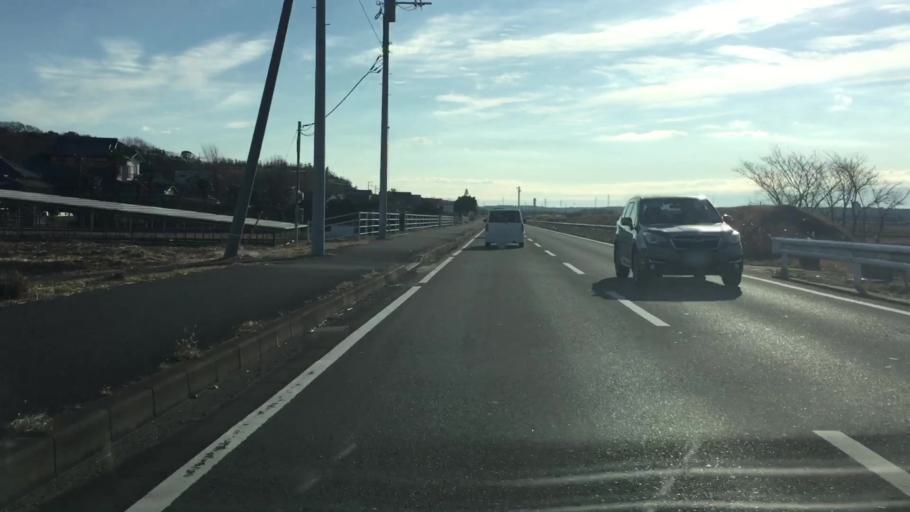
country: JP
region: Ibaraki
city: Toride
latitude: 35.8524
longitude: 140.1237
